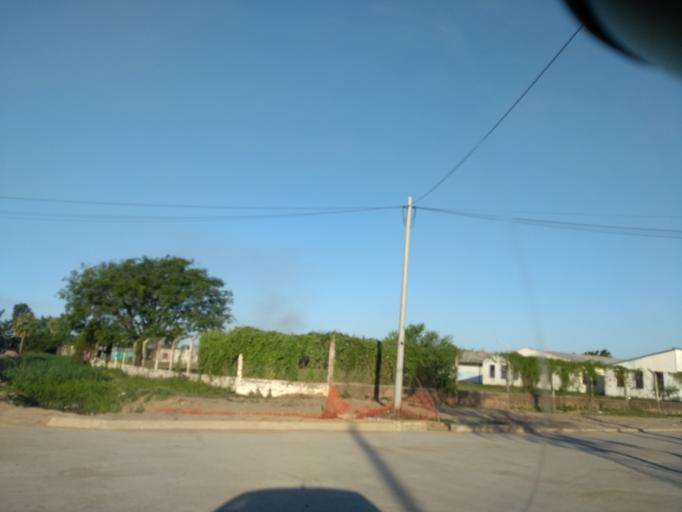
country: AR
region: Chaco
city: Barranqueras
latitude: -27.4800
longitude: -58.9454
